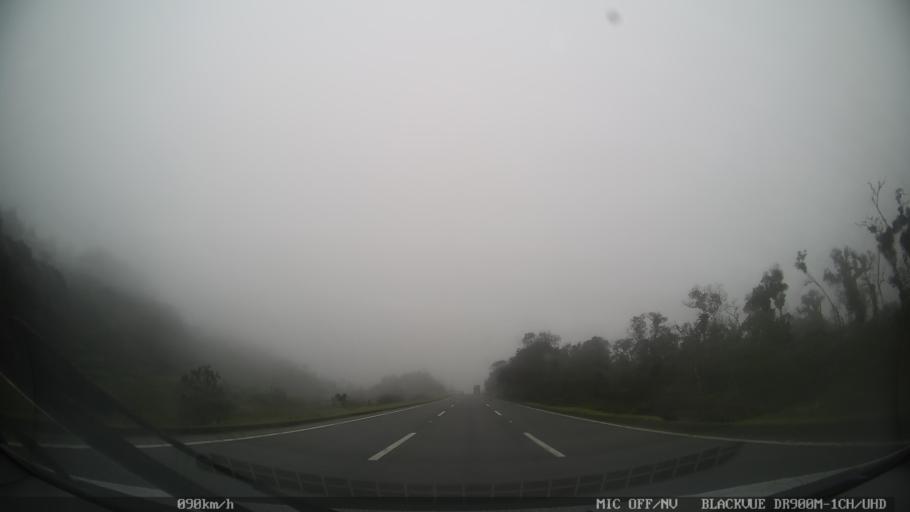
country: BR
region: Parana
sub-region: Antonina
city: Antonina
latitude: -25.1118
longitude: -48.7778
